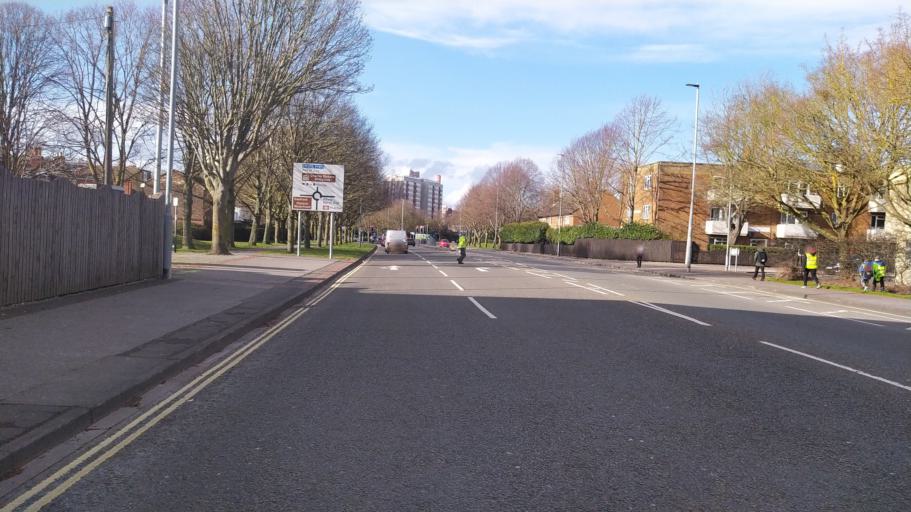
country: GB
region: England
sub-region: Portsmouth
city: Portsmouth
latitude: 50.8023
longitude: -1.0820
